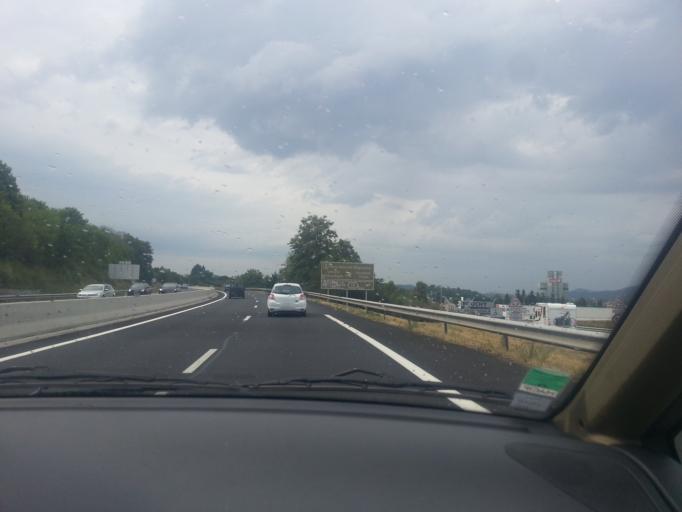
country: FR
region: Auvergne
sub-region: Departement du Puy-de-Dome
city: Issoire
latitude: 45.5181
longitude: 3.2603
